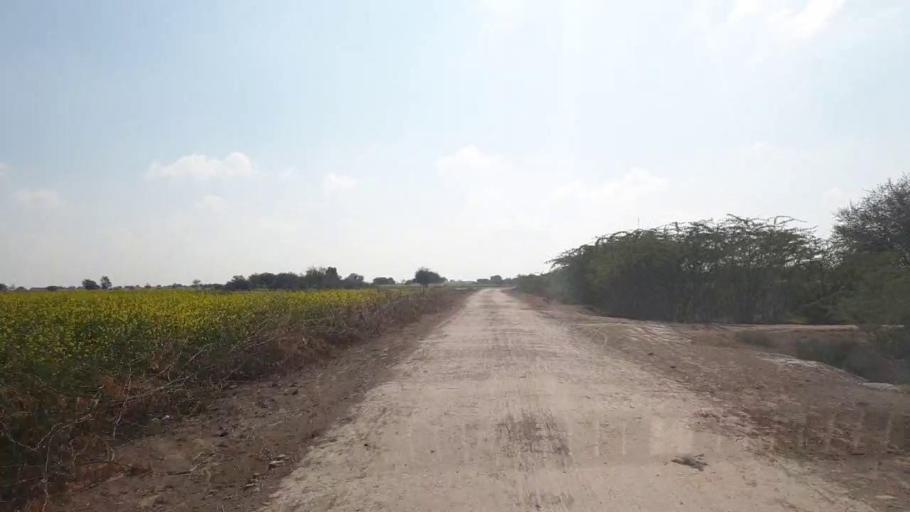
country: PK
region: Sindh
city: Shahpur Chakar
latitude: 26.0455
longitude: 68.6074
